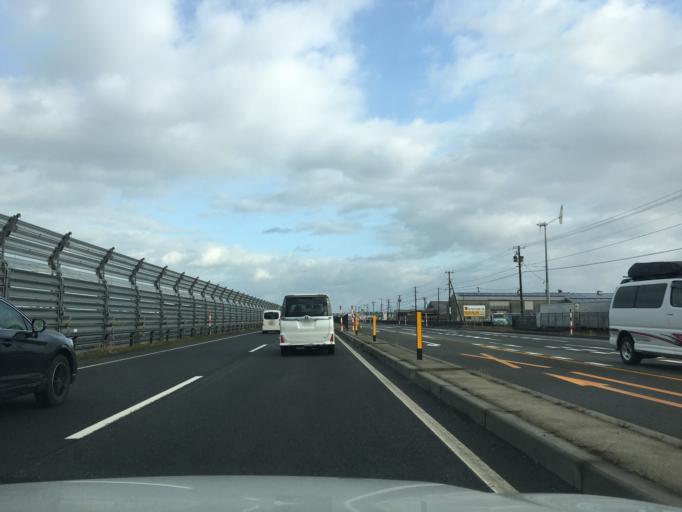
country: JP
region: Yamagata
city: Sakata
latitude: 38.8614
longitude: 139.8444
